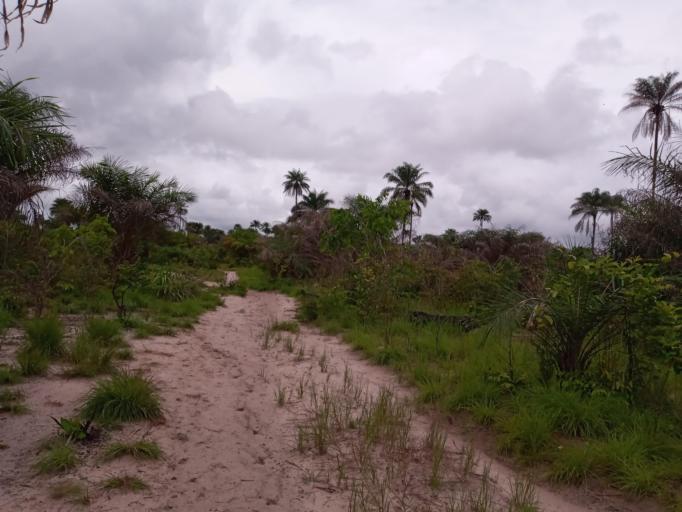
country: SL
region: Southern Province
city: Bonthe
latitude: 7.5206
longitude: -12.5734
